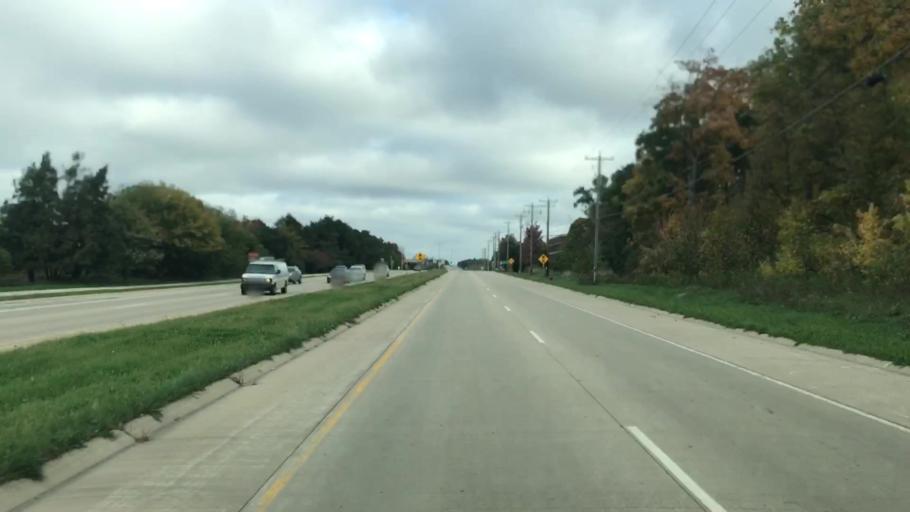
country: US
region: Wisconsin
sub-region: Waukesha County
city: Pewaukee
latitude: 43.0575
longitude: -88.2252
